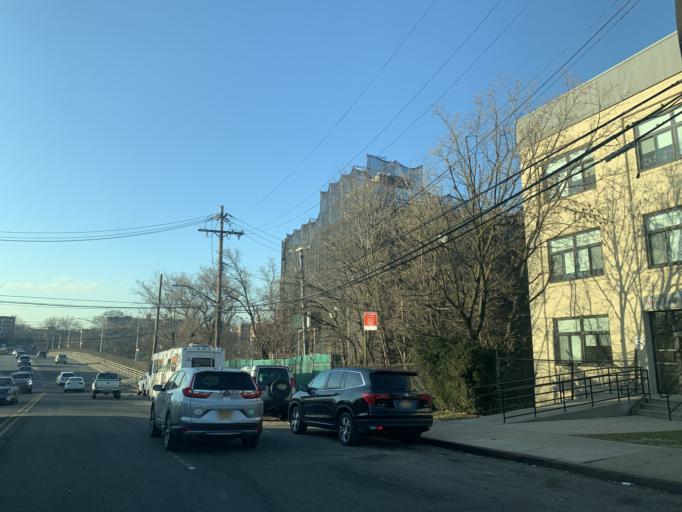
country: US
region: New York
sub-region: Westchester County
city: Mount Vernon
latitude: 40.8999
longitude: -73.8579
